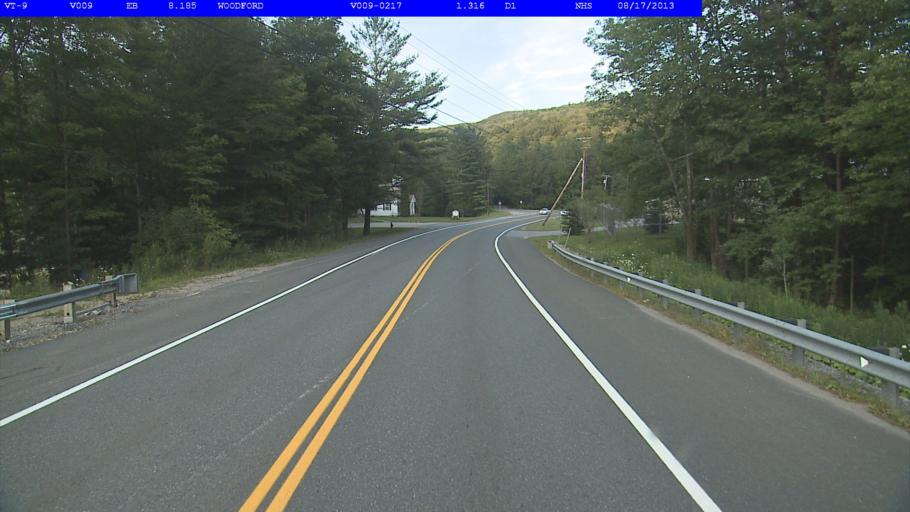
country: US
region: Vermont
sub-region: Bennington County
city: Bennington
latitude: 42.8962
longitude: -73.1316
